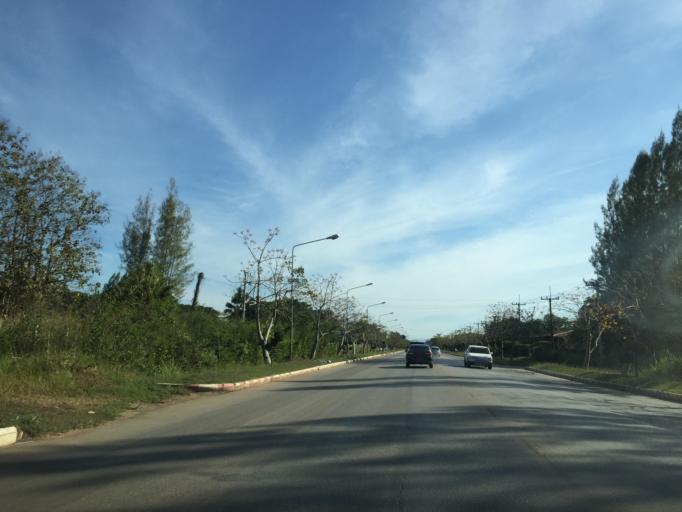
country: TH
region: Loei
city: Wang Saphung
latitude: 17.3195
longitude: 101.7616
